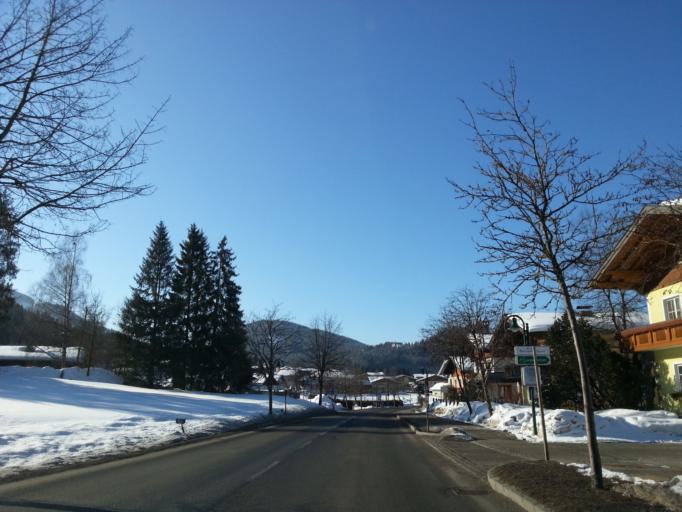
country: AT
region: Salzburg
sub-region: Politischer Bezirk Sankt Johann im Pongau
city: Eben im Pongau
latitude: 47.4638
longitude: 13.3808
